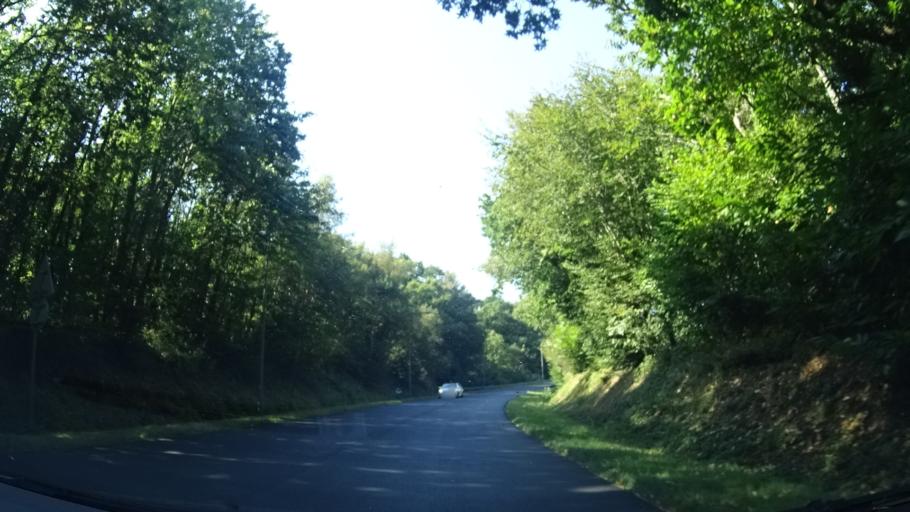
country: FR
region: Brittany
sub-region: Departement du Finistere
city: Douarnenez
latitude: 48.0861
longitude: -4.3424
